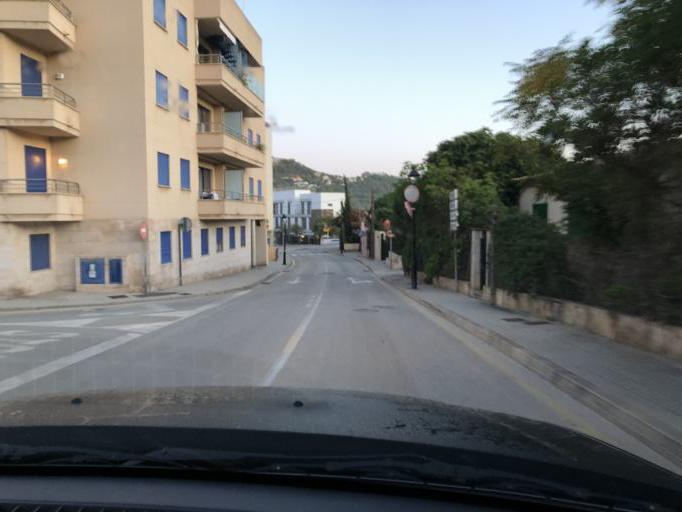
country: ES
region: Balearic Islands
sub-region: Illes Balears
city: Camp de Mar
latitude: 39.5448
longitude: 2.3927
